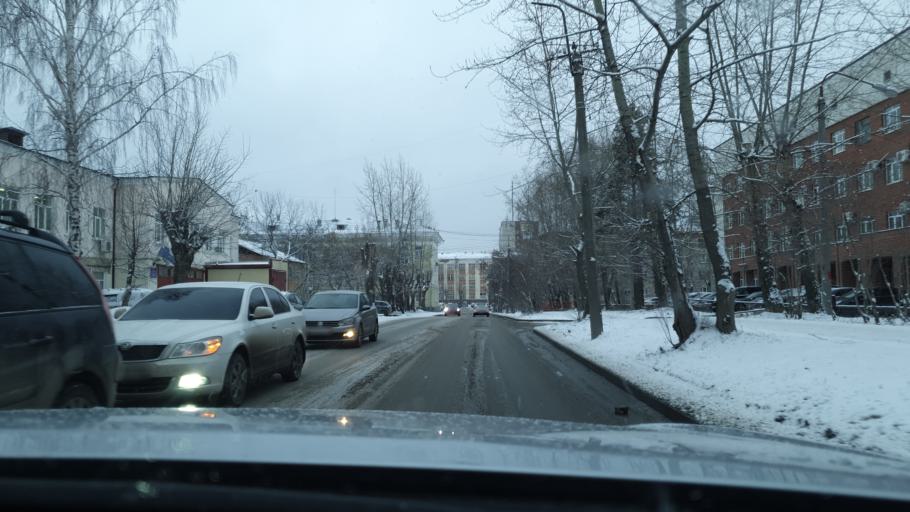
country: RU
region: Sverdlovsk
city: Istok
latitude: 56.7584
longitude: 60.7104
